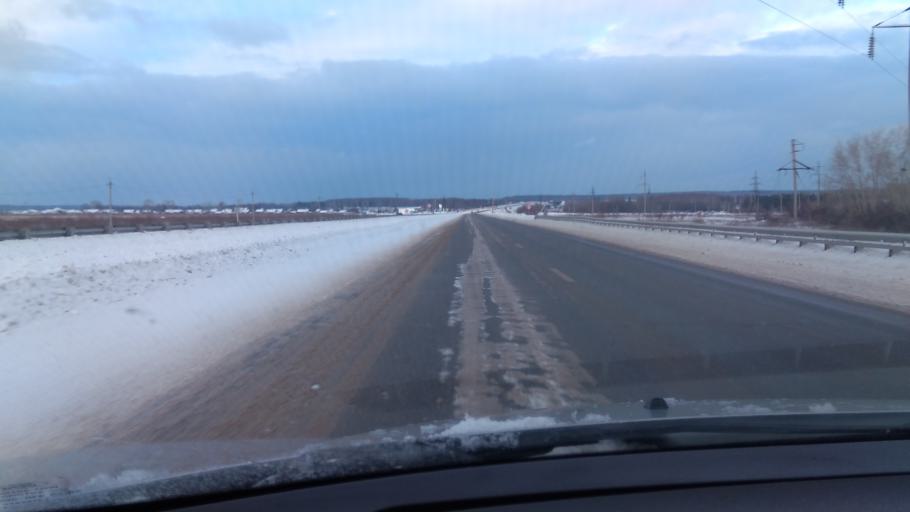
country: RU
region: Sverdlovsk
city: Tsementnyy
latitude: 57.4910
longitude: 60.1779
